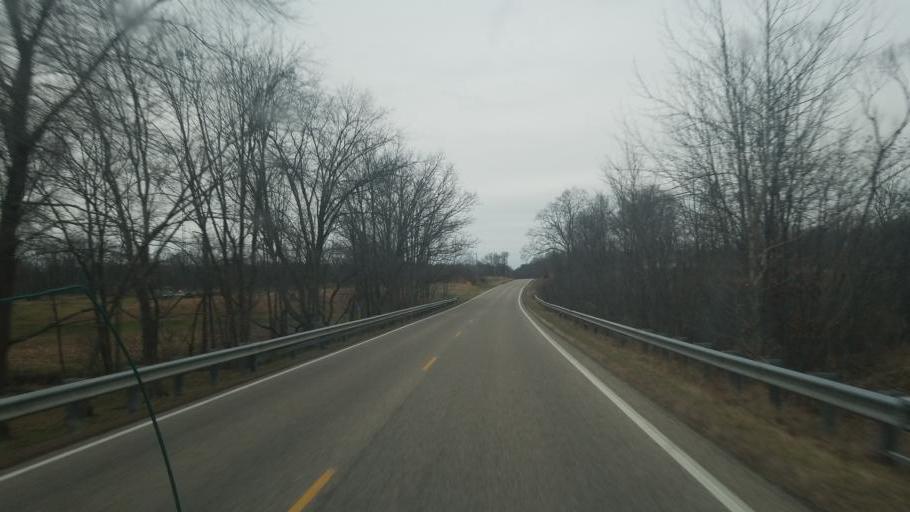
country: US
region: Indiana
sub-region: Clay County
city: Middlebury
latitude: 39.3612
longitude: -86.9541
